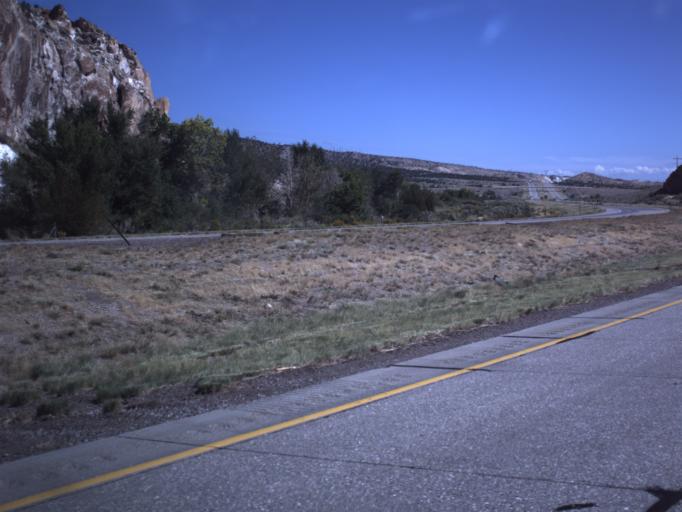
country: US
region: Utah
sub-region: Sevier County
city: Monroe
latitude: 38.5794
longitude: -112.2818
